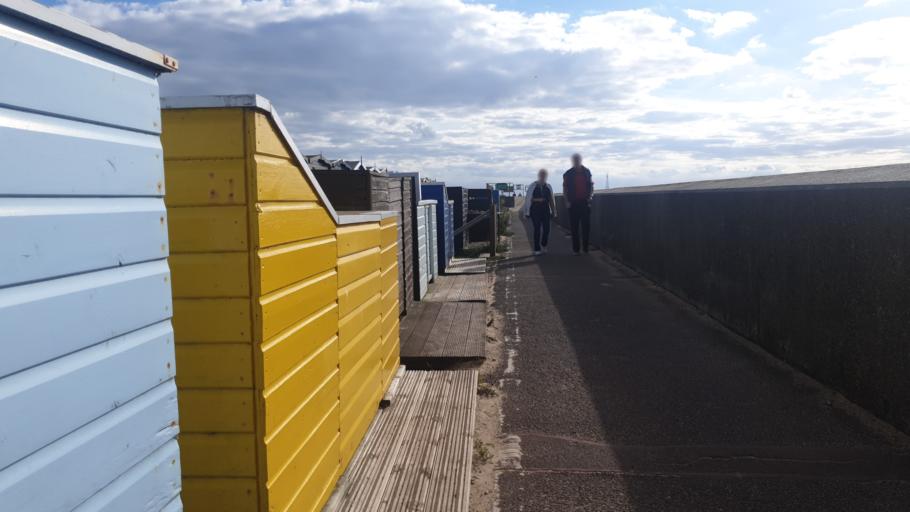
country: GB
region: England
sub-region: Essex
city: Frinton-on-Sea
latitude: 51.8218
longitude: 1.2394
